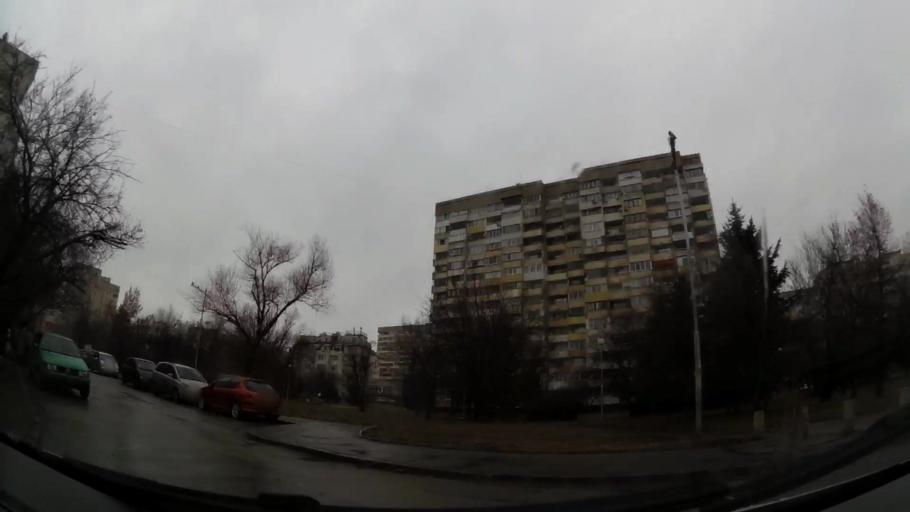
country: BG
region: Sofia-Capital
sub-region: Stolichna Obshtina
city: Sofia
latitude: 42.6431
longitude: 23.3704
